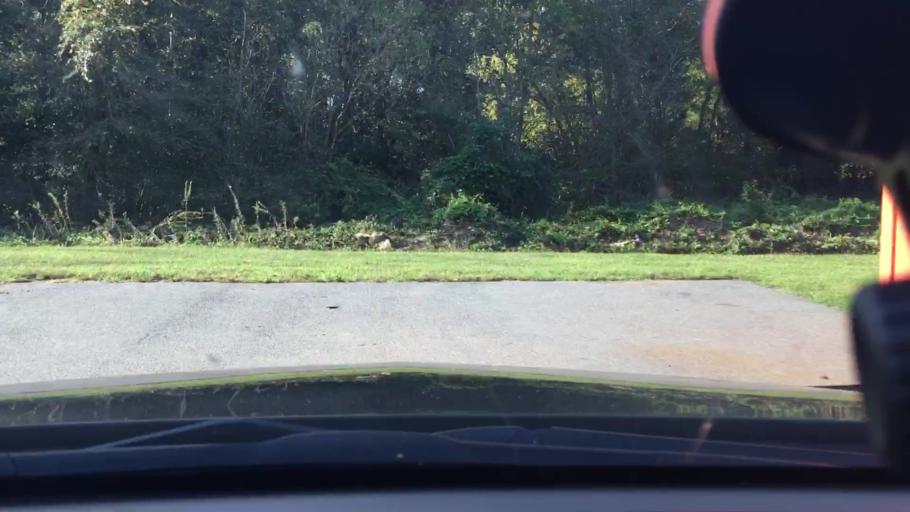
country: US
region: North Carolina
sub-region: Stanly County
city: Albemarle
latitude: 35.3721
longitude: -80.1966
